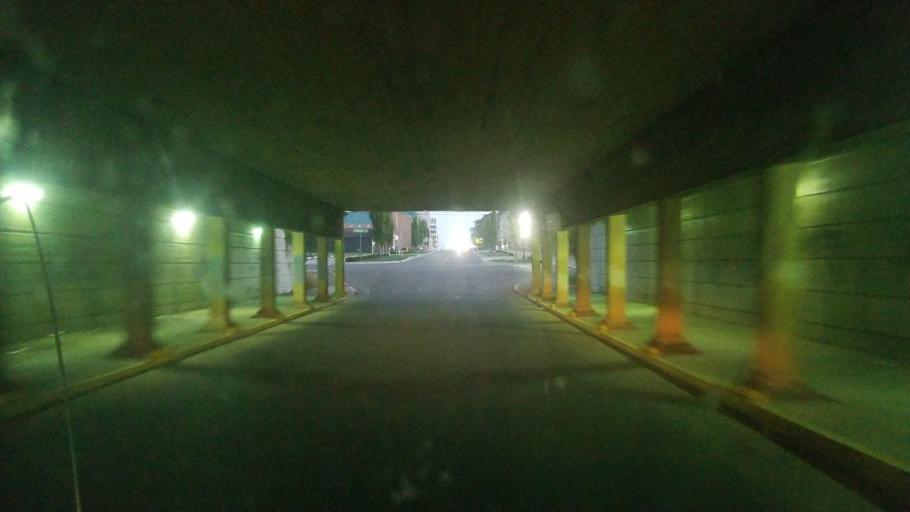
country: US
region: Ohio
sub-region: Licking County
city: Newark
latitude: 40.0548
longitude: -82.4012
